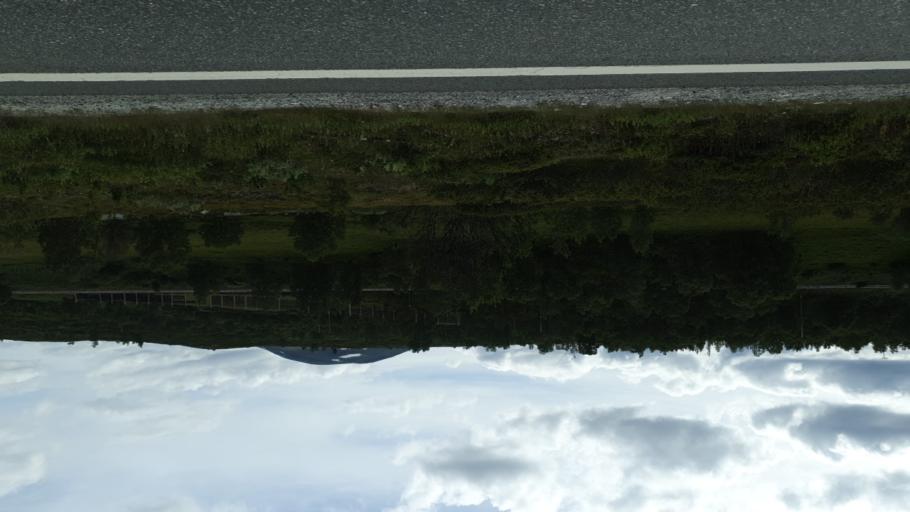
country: NO
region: Sor-Trondelag
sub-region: Oppdal
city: Oppdal
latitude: 62.2739
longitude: 9.5838
